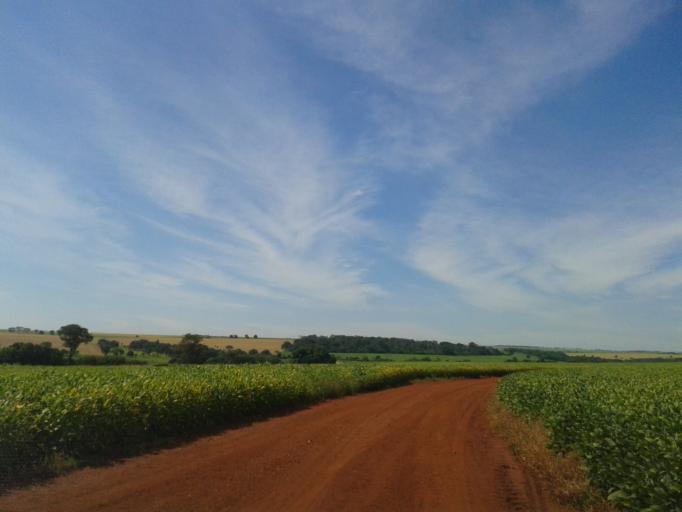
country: BR
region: Minas Gerais
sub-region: Capinopolis
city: Capinopolis
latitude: -18.6465
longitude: -49.7136
